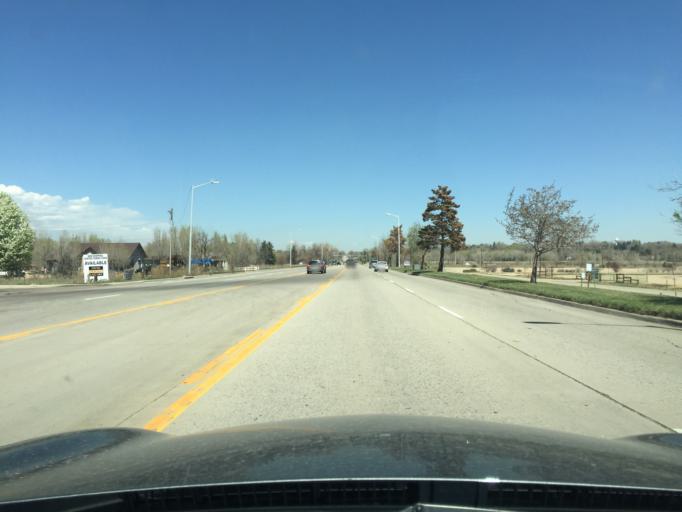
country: US
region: Colorado
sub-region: Boulder County
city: Longmont
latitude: 40.1557
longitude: -105.1306
